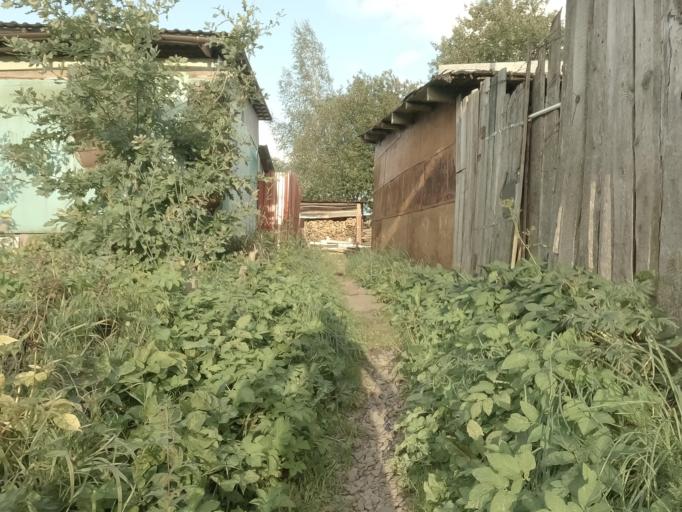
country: RU
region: Leningrad
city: Mga
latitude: 59.7513
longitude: 31.0365
